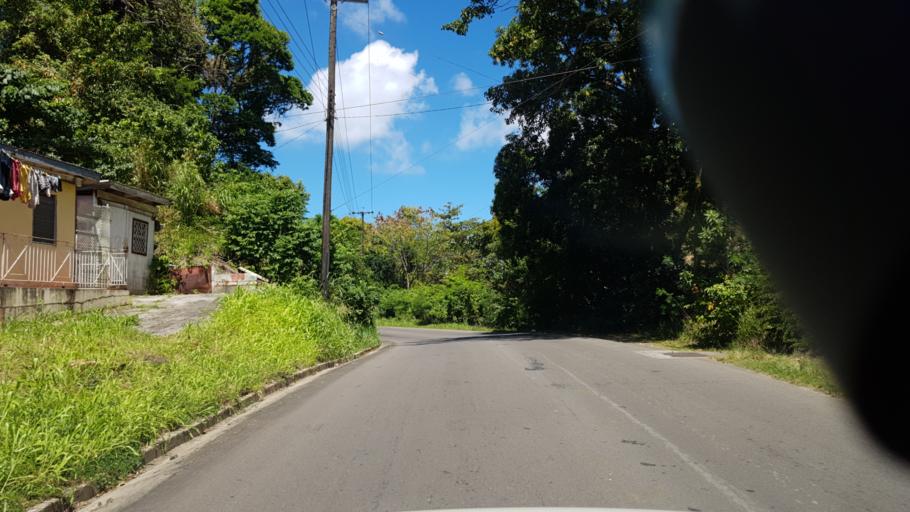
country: LC
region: Castries Quarter
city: Bisee
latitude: 14.0299
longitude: -60.9640
